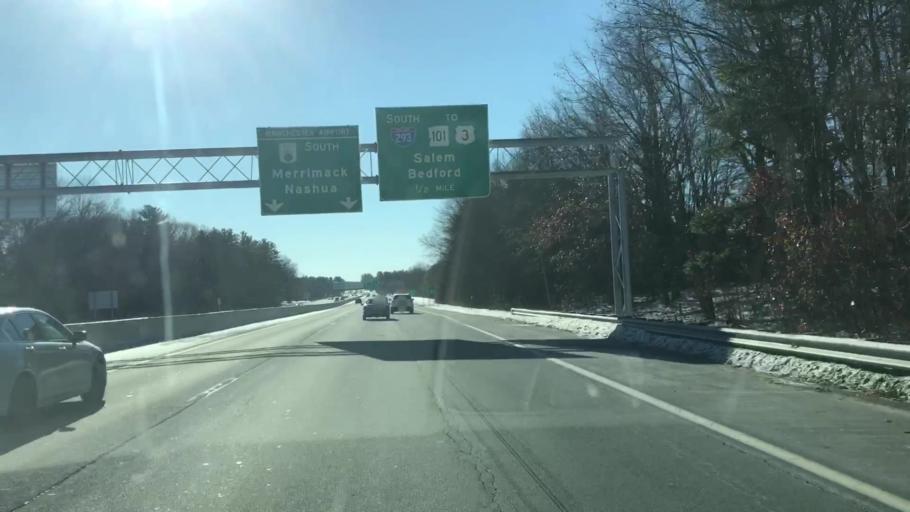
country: US
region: New Hampshire
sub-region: Hillsborough County
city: Manchester
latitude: 42.9615
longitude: -71.4759
